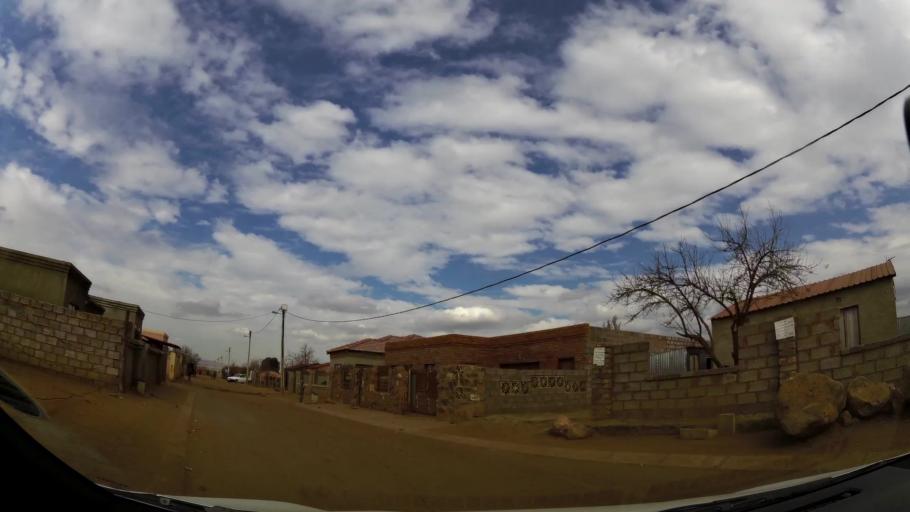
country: ZA
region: Gauteng
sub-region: Ekurhuleni Metropolitan Municipality
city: Germiston
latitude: -26.4142
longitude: 28.1596
